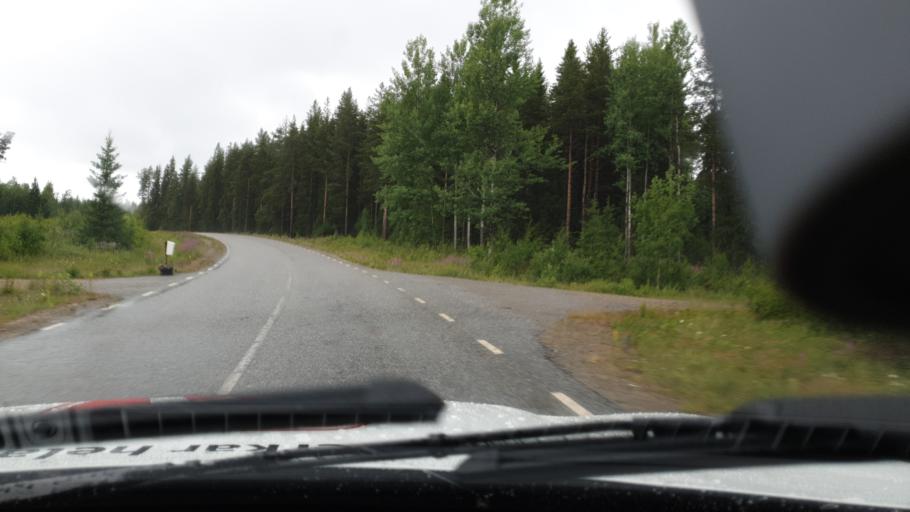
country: SE
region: Vaesterbotten
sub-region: Skelleftea Kommun
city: Langsele
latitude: 64.6881
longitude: 20.0285
